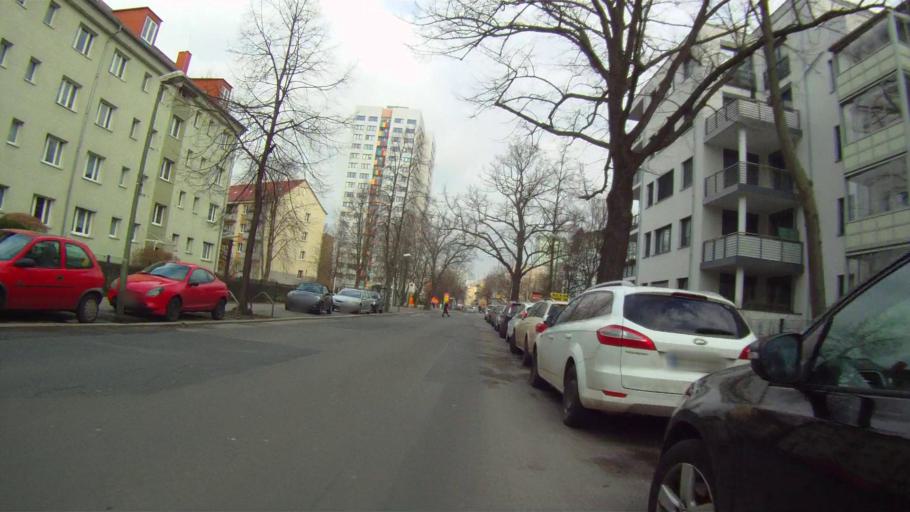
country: DE
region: Berlin
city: Friedrichsfelde
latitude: 52.5061
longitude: 13.5118
